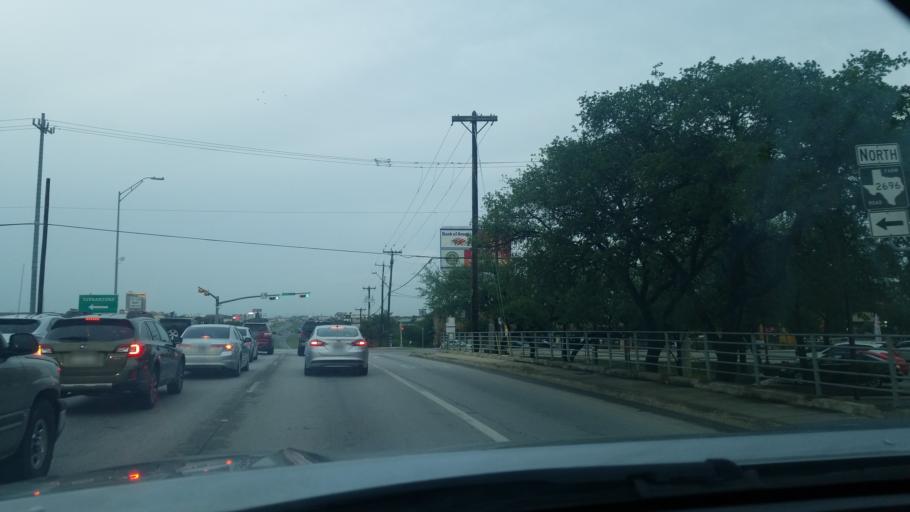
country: US
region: Texas
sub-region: Bexar County
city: Hollywood Park
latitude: 29.6082
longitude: -98.5090
